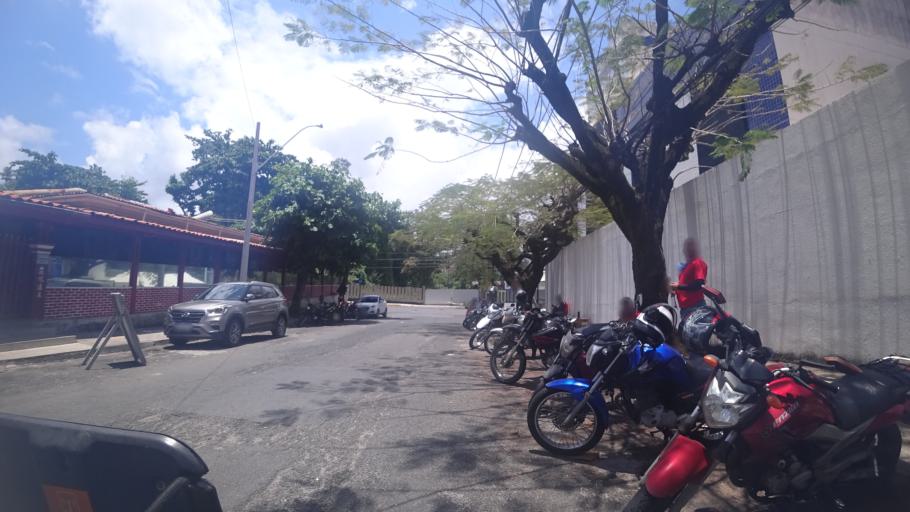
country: BR
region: Bahia
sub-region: Salvador
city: Salvador
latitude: -12.9996
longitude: -38.4571
